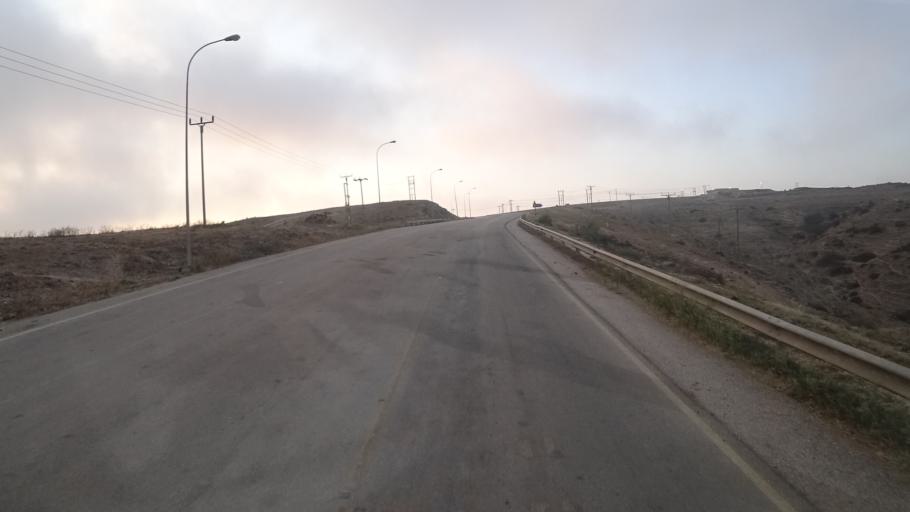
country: OM
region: Zufar
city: Salalah
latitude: 17.1213
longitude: 53.9291
